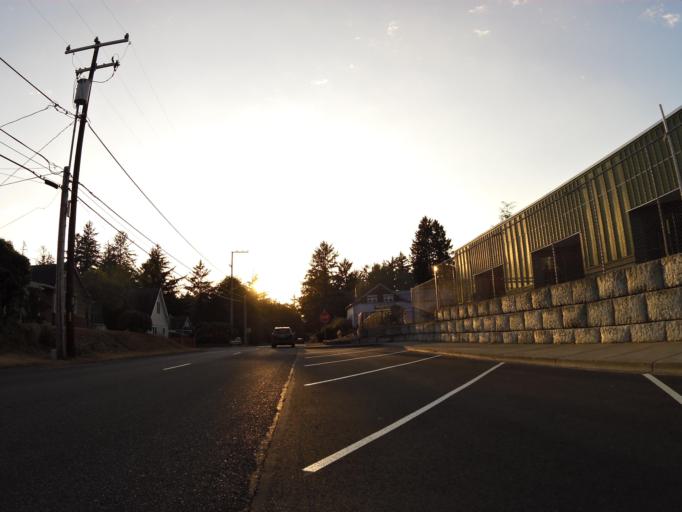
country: US
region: Oregon
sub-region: Clatsop County
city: Warrenton
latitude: 46.1577
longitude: -123.9315
